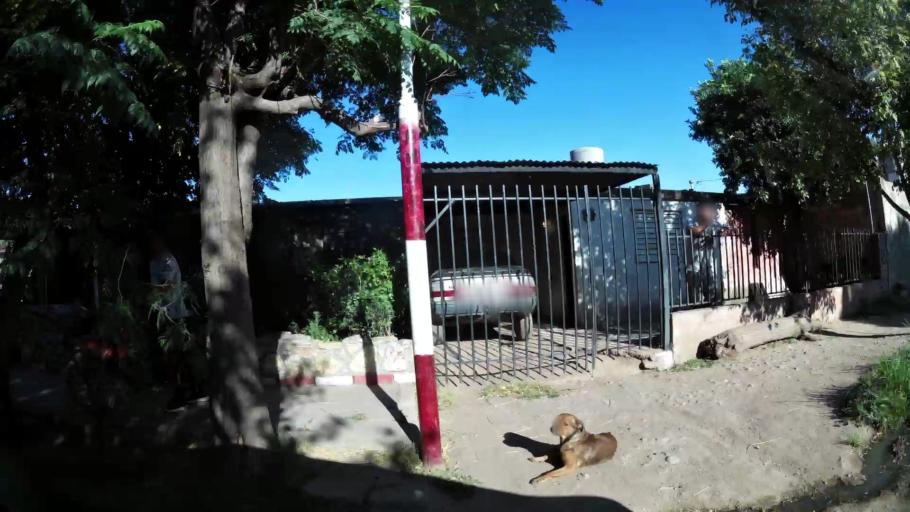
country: AR
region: Cordoba
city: Villa Allende
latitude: -31.3332
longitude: -64.2410
